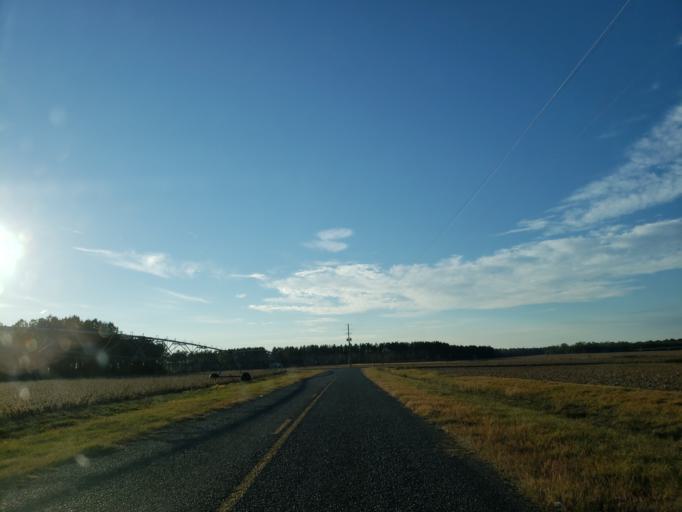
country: US
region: Georgia
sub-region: Dooly County
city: Unadilla
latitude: 32.2078
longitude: -83.7965
